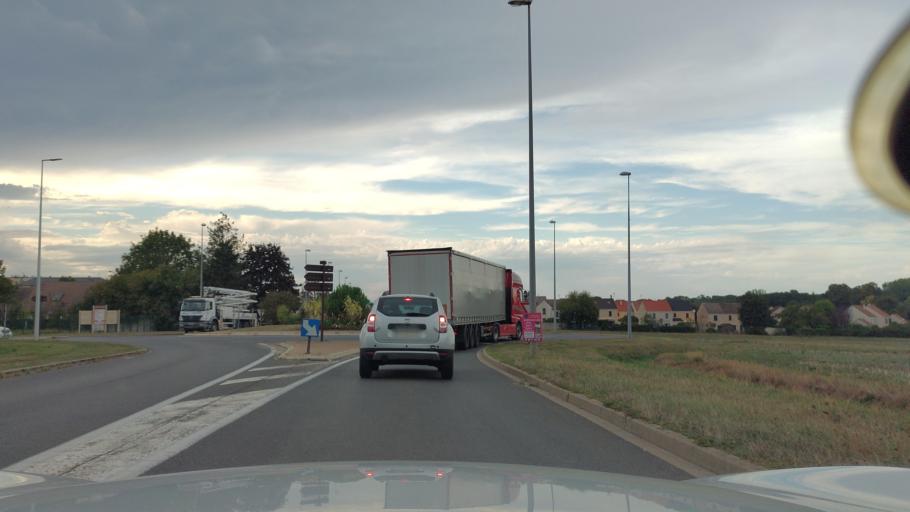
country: FR
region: Ile-de-France
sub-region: Departement de Seine-et-Marne
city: Guignes
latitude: 48.6309
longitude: 2.8102
